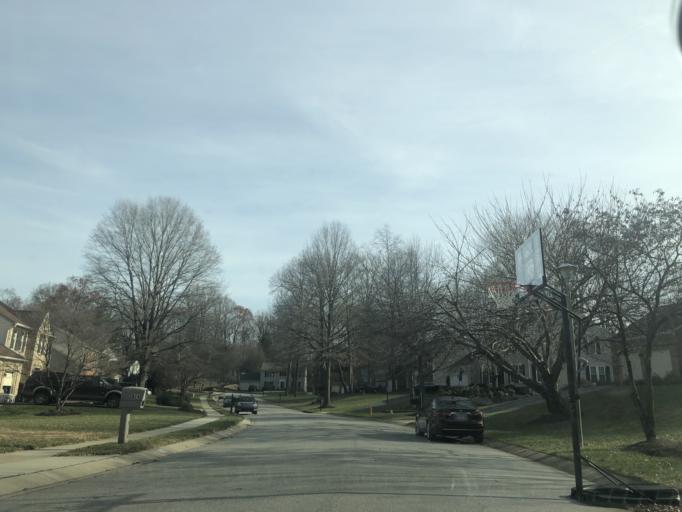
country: US
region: Maryland
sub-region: Howard County
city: Columbia
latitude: 39.2923
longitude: -76.8442
